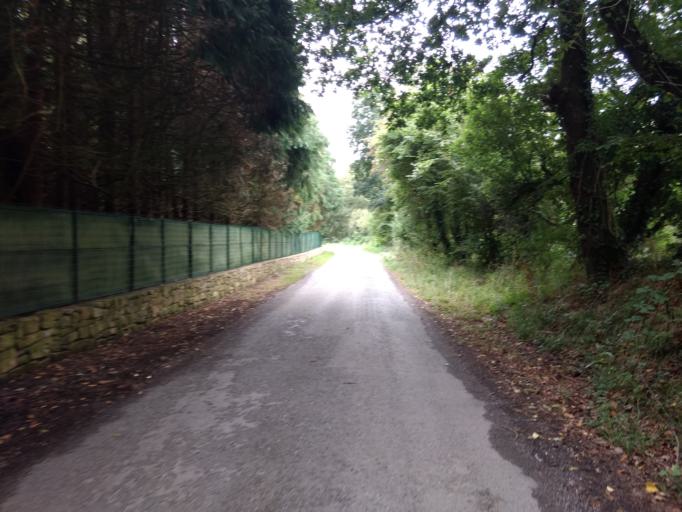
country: FR
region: Brittany
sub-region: Departement du Finistere
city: Loperhet
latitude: 48.3565
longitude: -4.2946
